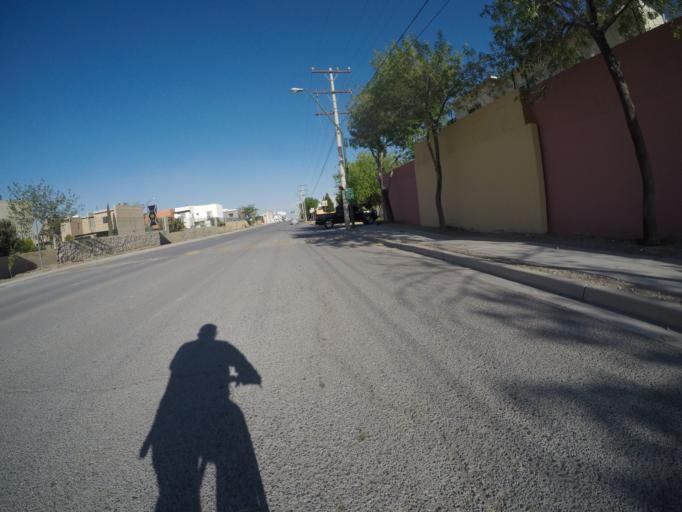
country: US
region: Texas
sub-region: El Paso County
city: Socorro
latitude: 31.6997
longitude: -106.3861
